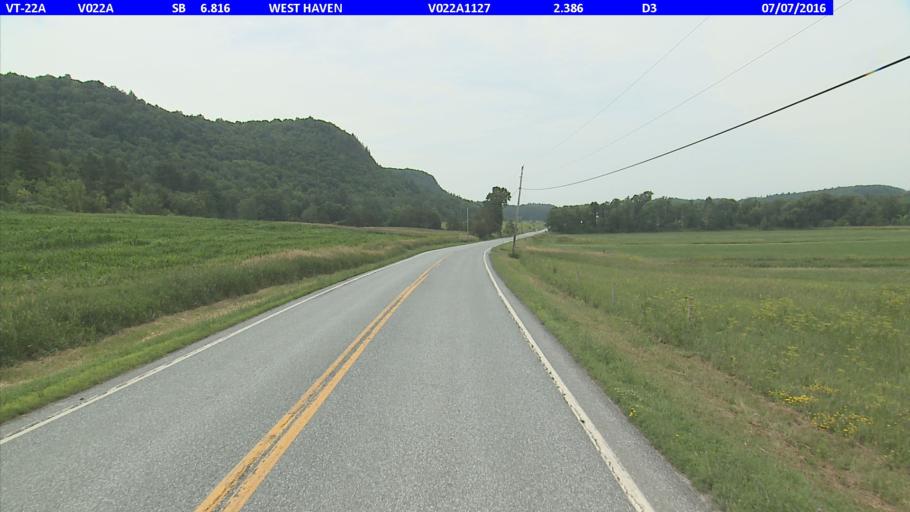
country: US
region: Vermont
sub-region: Rutland County
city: Fair Haven
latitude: 43.6607
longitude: -73.2912
